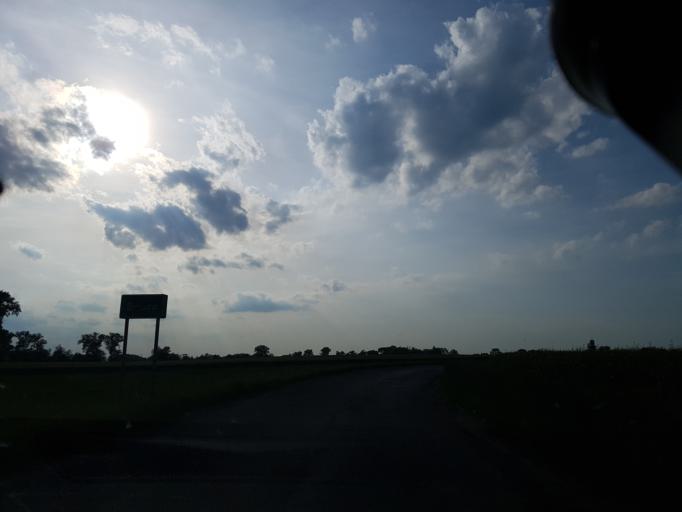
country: PL
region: Lower Silesian Voivodeship
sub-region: Powiat wroclawski
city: Zorawina
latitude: 50.9105
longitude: 17.0033
